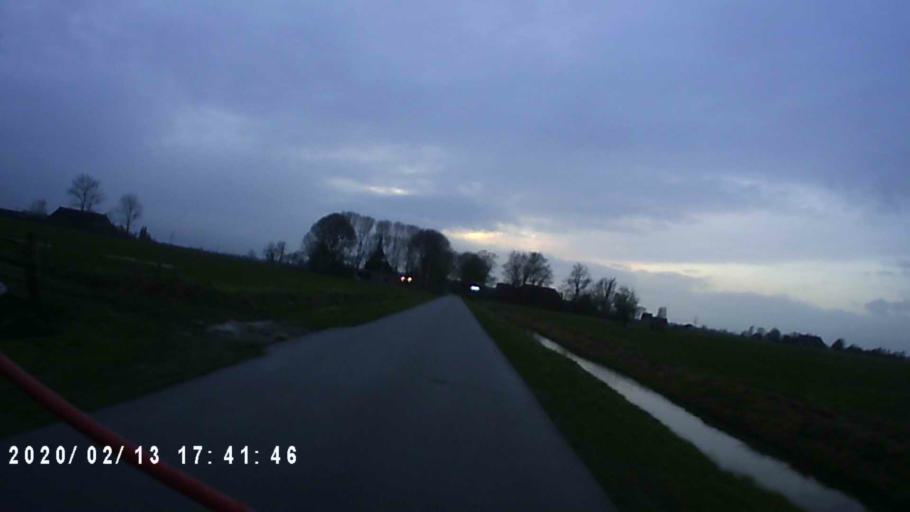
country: NL
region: Groningen
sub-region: Gemeente Zuidhorn
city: Aduard
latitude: 53.2295
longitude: 6.4940
